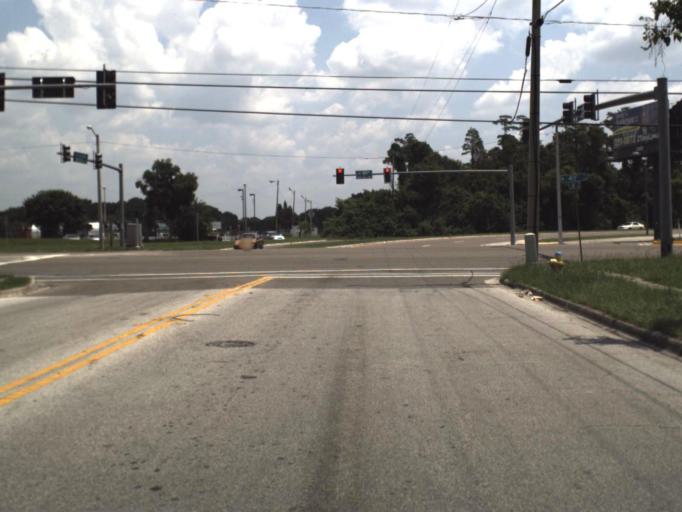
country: US
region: Florida
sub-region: Hillsborough County
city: East Lake-Orient Park
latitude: 27.9741
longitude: -82.4146
